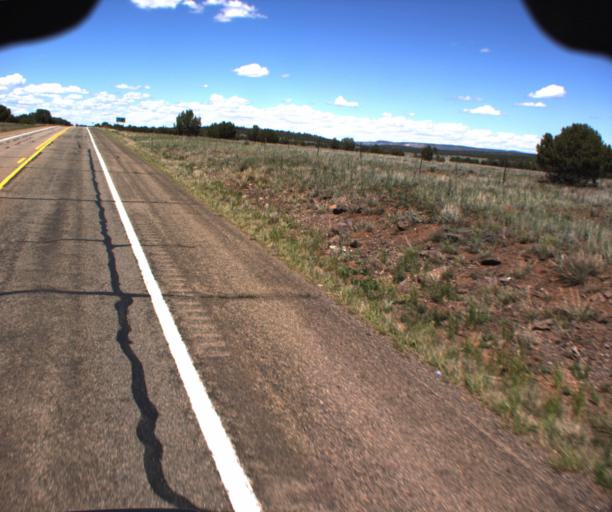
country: US
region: Arizona
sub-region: Yavapai County
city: Paulden
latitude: 35.1441
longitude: -112.4458
